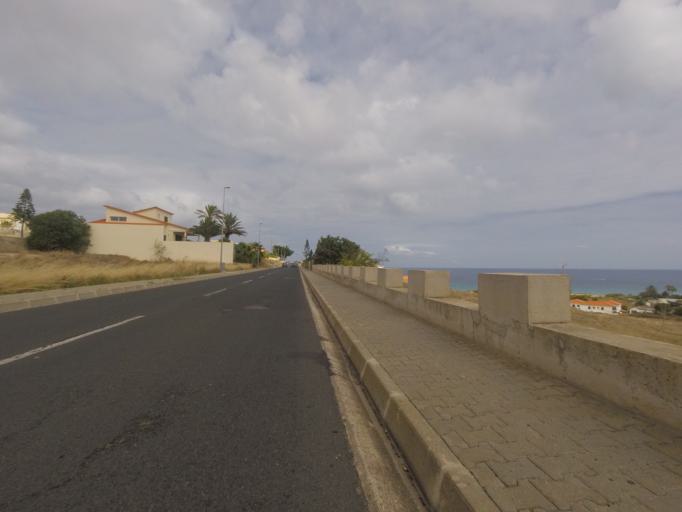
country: PT
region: Madeira
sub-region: Porto Santo
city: Vila de Porto Santo
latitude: 33.0546
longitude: -16.3477
